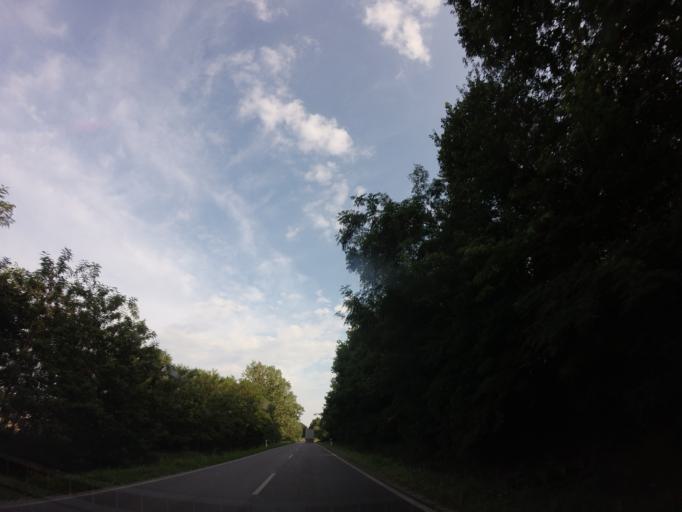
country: PL
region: Lublin Voivodeship
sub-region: Powiat lubartowski
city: Michow
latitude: 51.5401
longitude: 22.3061
